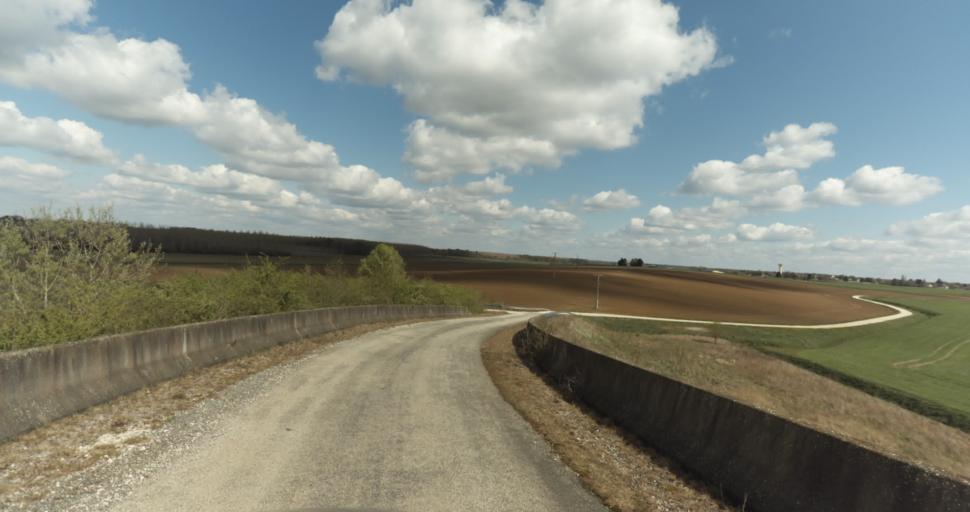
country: FR
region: Bourgogne
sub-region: Departement de la Cote-d'Or
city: Auxonne
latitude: 47.2234
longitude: 5.4254
